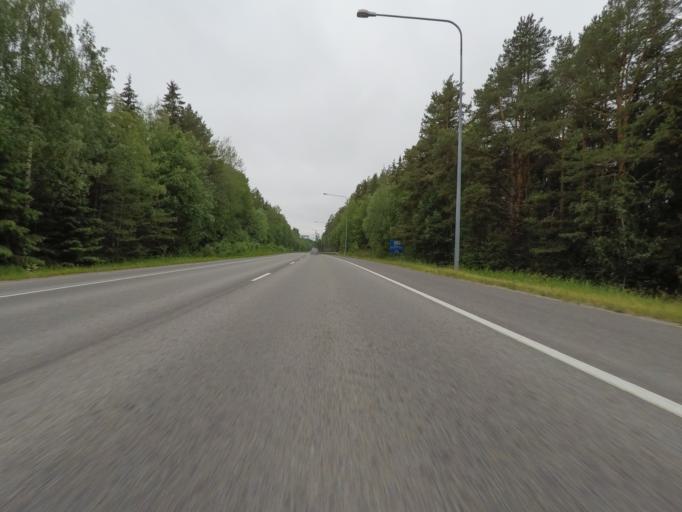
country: FI
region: Varsinais-Suomi
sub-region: Turku
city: Raisio
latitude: 60.4613
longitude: 22.1701
